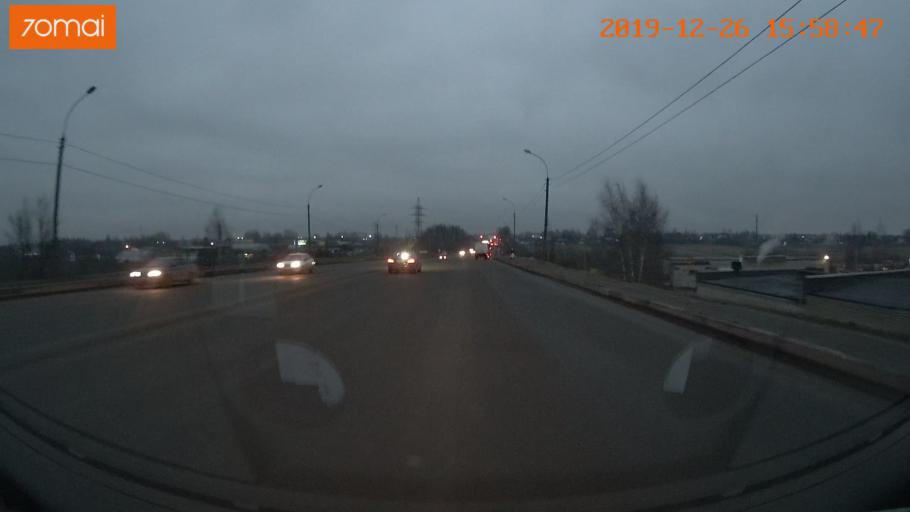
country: RU
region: Jaroslavl
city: Rybinsk
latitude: 58.0366
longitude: 38.7986
